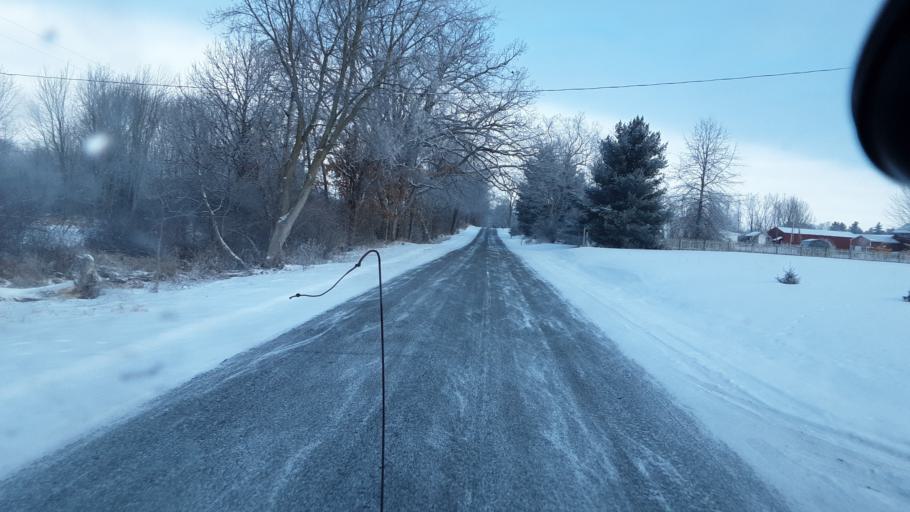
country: US
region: Michigan
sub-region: Ingham County
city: Leslie
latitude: 42.4445
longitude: -84.4970
